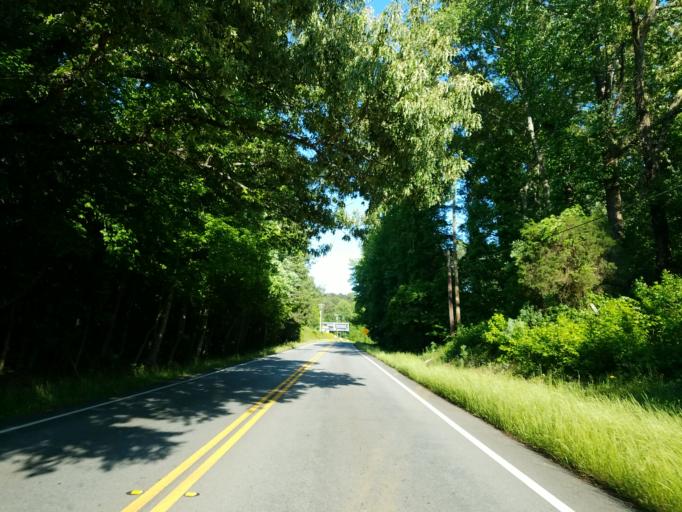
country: US
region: Georgia
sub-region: Carroll County
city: Villa Rica
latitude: 33.7318
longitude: -84.8407
